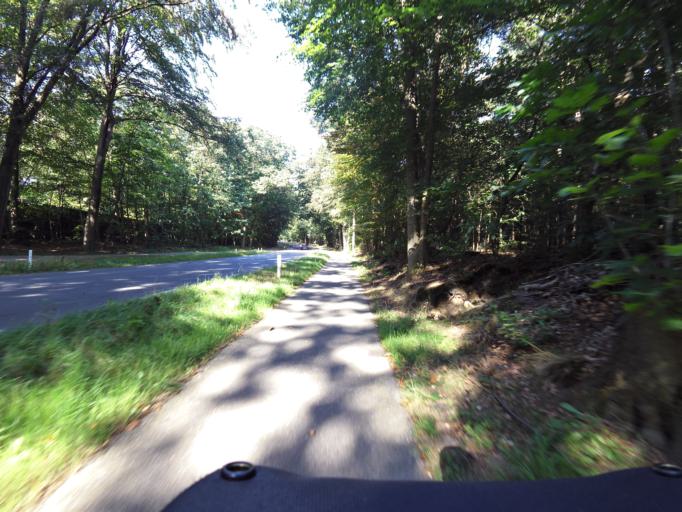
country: NL
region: Gelderland
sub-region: Gemeente Apeldoorn
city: Apeldoorn
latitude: 52.2158
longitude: 5.9214
